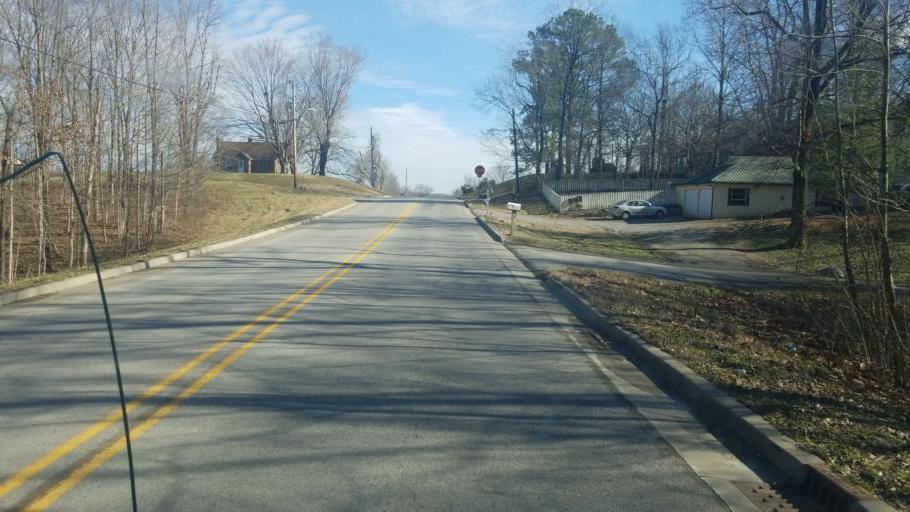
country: US
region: Illinois
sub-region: Jackson County
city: Carbondale
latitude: 37.7006
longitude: -89.1960
